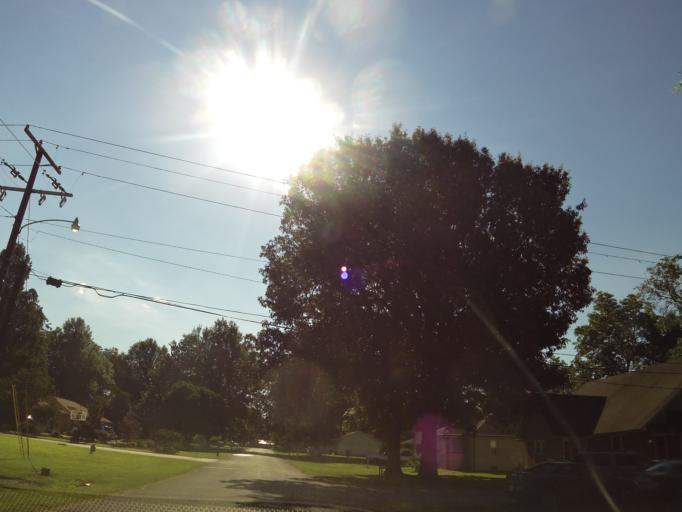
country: US
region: Arkansas
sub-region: Clay County
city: Corning
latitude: 36.4077
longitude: -90.5902
